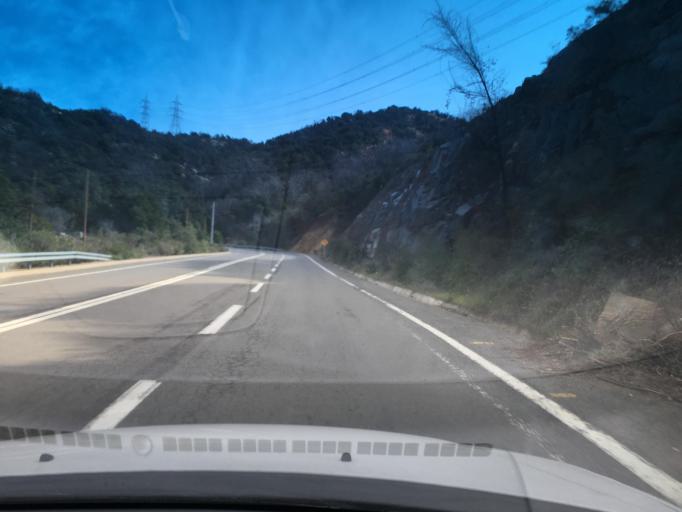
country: CL
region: Valparaiso
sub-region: Provincia de San Felipe
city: Llaillay
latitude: -33.0575
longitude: -71.0022
